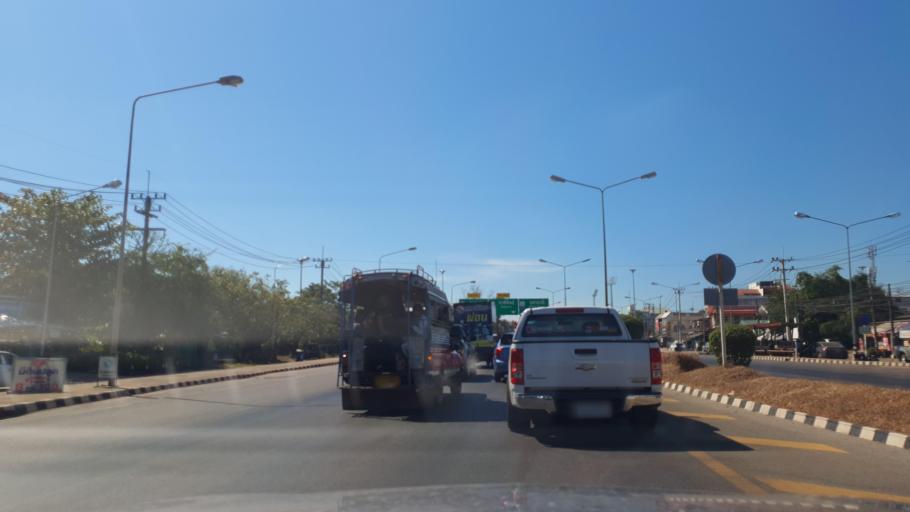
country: TH
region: Sakon Nakhon
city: Sakon Nakhon
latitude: 17.1938
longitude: 104.0966
